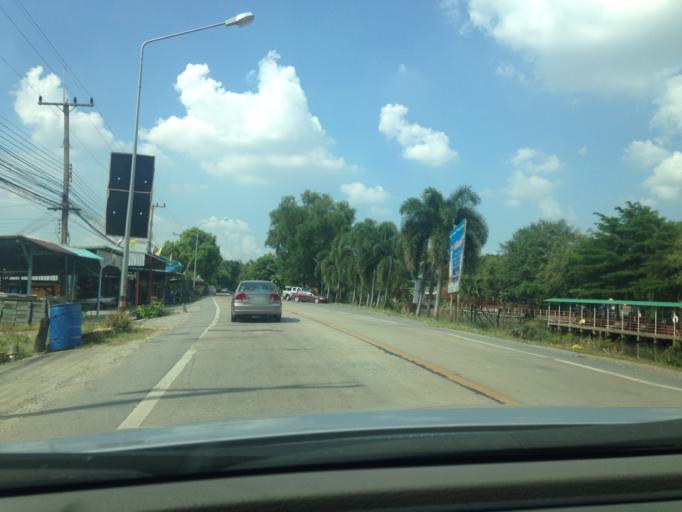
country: TH
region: Pathum Thani
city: Khlong Luang
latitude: 14.0595
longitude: 100.5895
